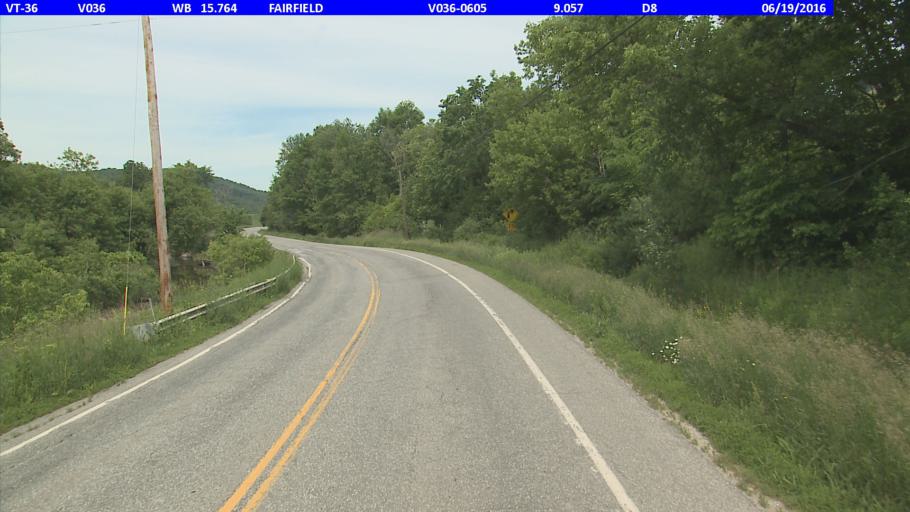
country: US
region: Vermont
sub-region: Franklin County
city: Enosburg Falls
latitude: 44.7885
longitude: -72.8654
